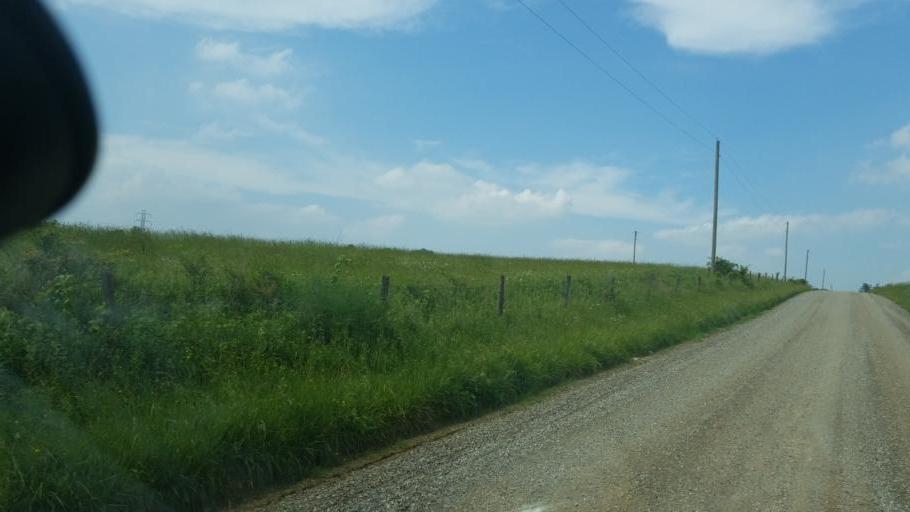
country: US
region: Ohio
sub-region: Knox County
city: Oak Hill
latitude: 40.2987
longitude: -82.2126
